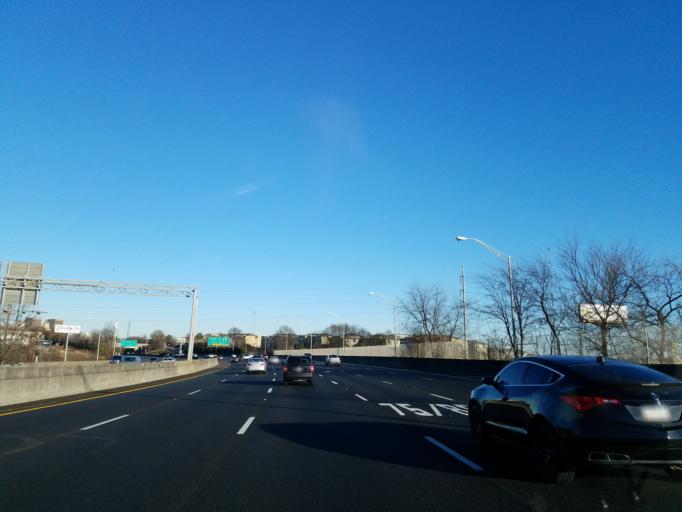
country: US
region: Georgia
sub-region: Fulton County
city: Atlanta
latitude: 33.7410
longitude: -84.4096
